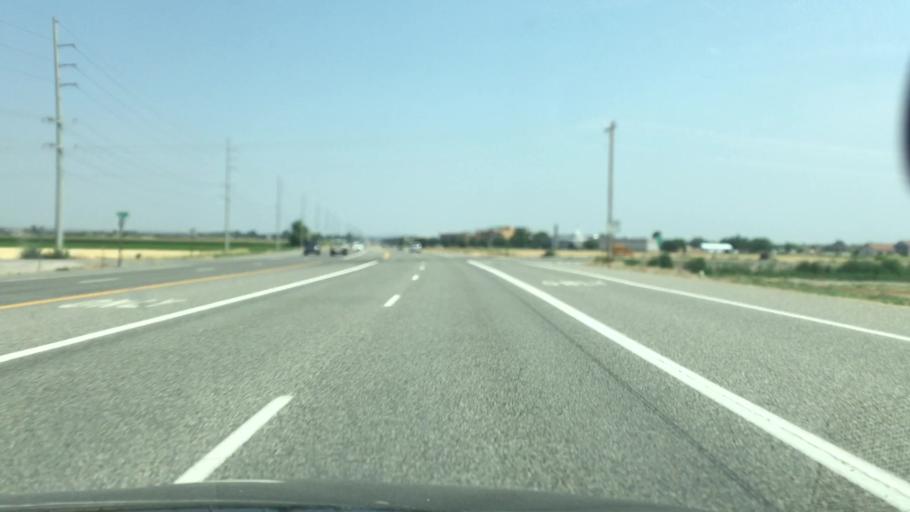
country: US
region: Idaho
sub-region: Twin Falls County
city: Twin Falls
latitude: 42.5917
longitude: -114.5101
